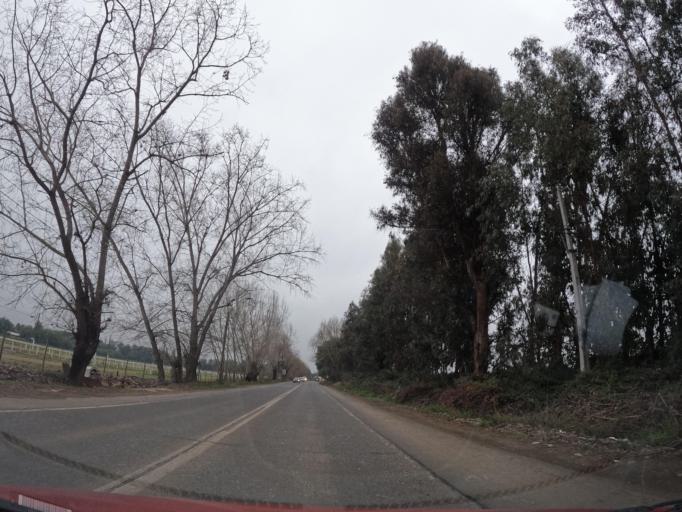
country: CL
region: Maule
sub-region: Provincia de Talca
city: San Clemente
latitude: -35.5563
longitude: -71.4662
